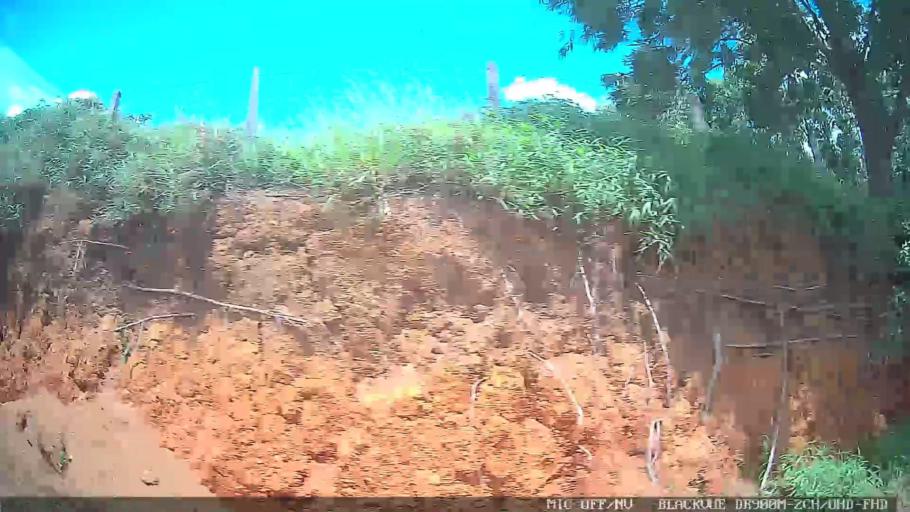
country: BR
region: Minas Gerais
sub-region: Extrema
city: Extrema
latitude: -22.7464
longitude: -46.4328
